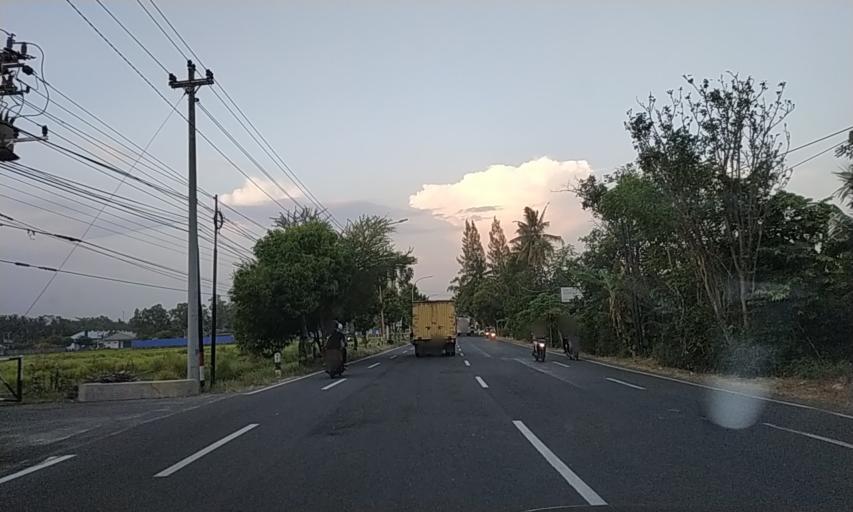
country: ID
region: Daerah Istimewa Yogyakarta
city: Srandakan
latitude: -7.8740
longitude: 110.1369
